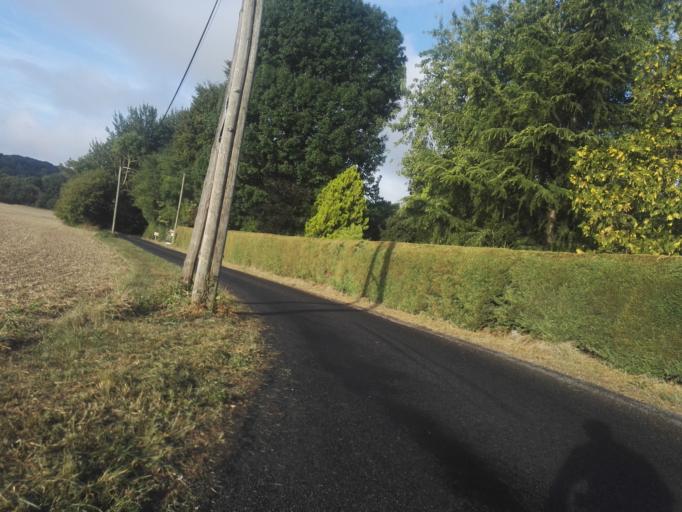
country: FR
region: Haute-Normandie
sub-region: Departement de l'Eure
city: Menilles
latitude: 49.0366
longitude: 1.3464
